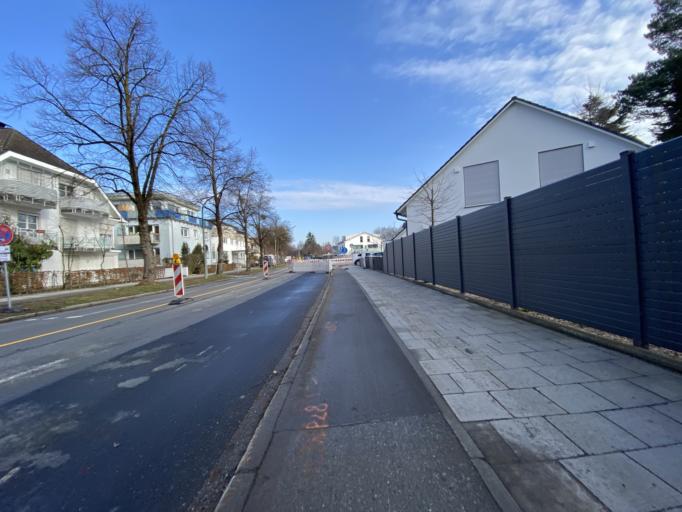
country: DE
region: Bavaria
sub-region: Upper Bavaria
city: Bogenhausen
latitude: 48.1425
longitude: 11.6277
